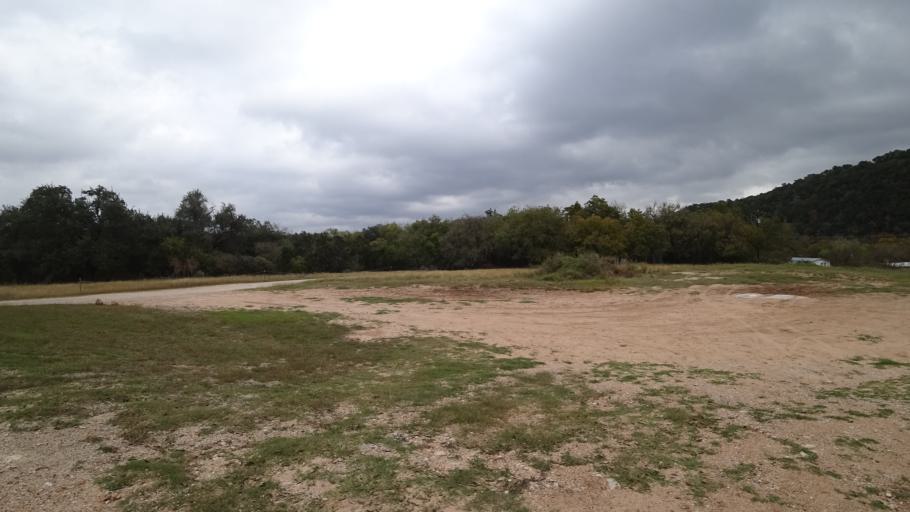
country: US
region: Texas
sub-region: Travis County
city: Bee Cave
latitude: 30.3284
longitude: -97.9185
